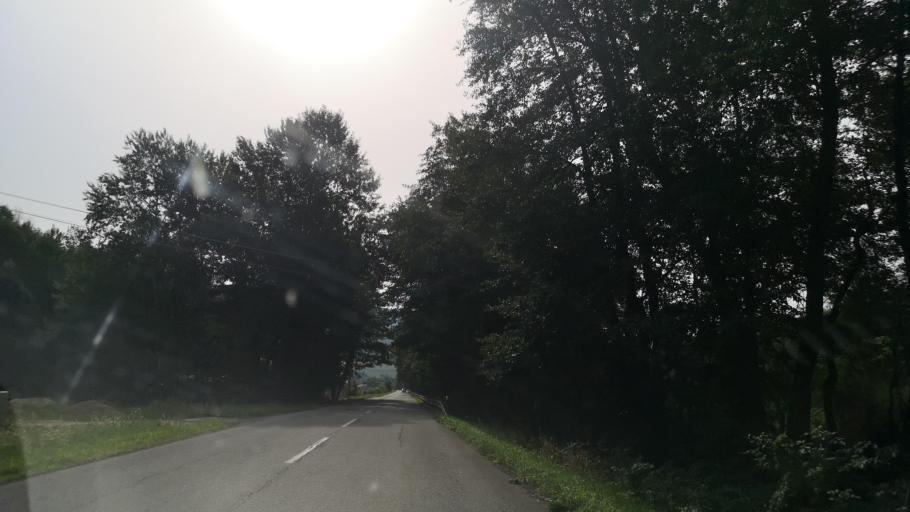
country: SK
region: Banskobystricky
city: Poltar
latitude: 48.5742
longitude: 19.8291
